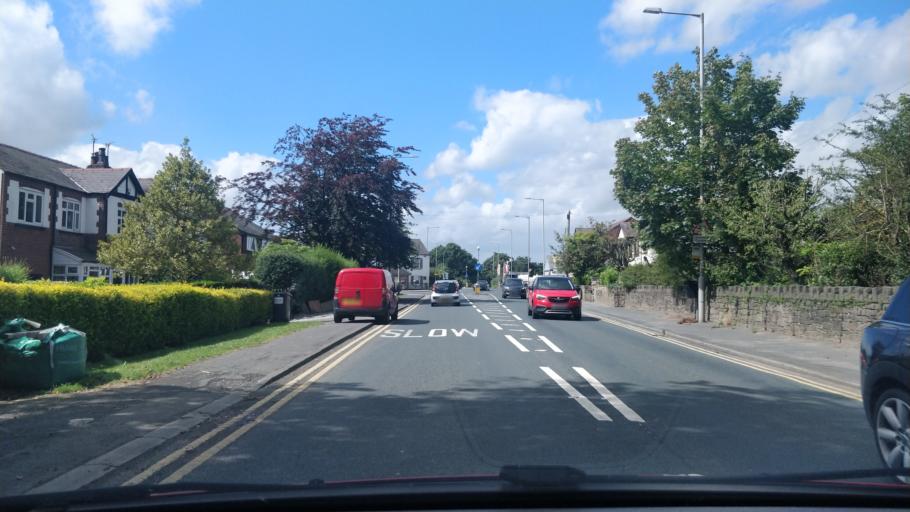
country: GB
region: England
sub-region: Lancashire
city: Appley Bridge
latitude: 53.5918
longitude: -2.7233
